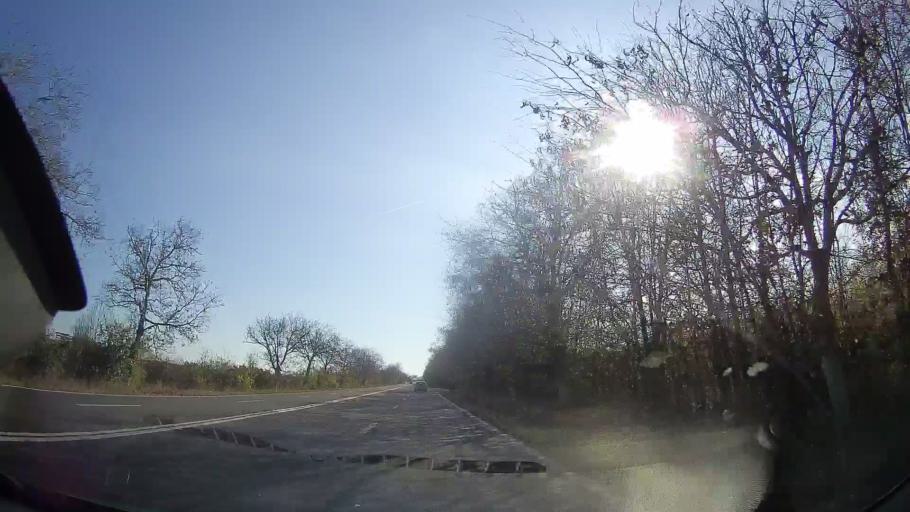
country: RO
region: Constanta
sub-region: Comuna Douazeci si Trei August
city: Douazeci si Trei August
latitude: 43.8920
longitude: 28.5722
